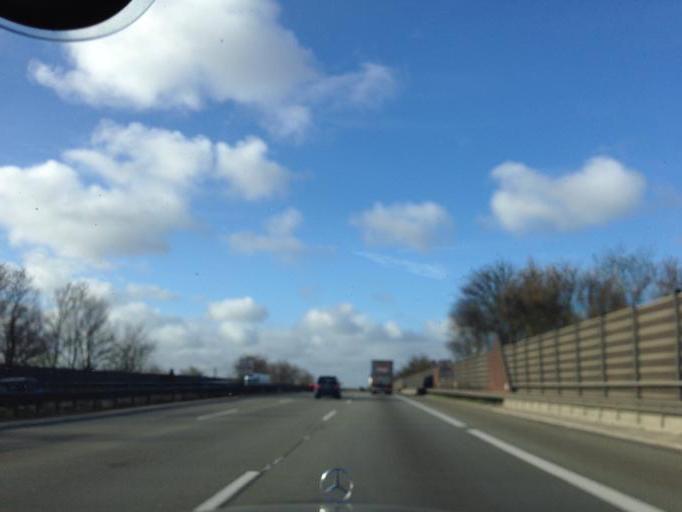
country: DE
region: Hamburg
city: Harburg
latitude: 53.4234
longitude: 10.0333
